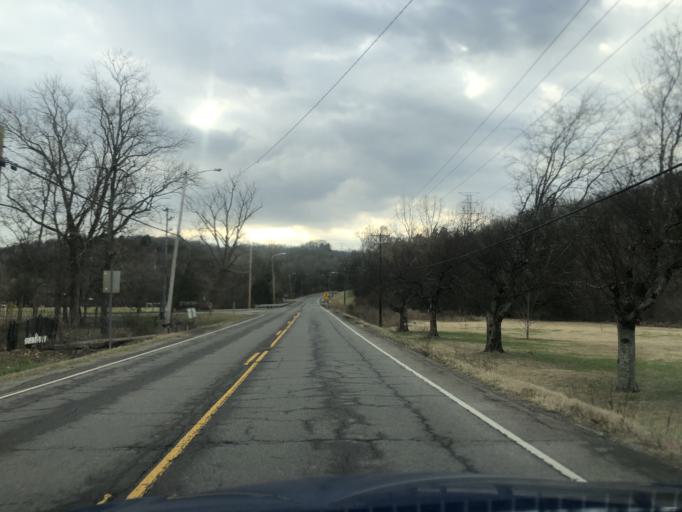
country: US
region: Tennessee
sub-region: Davidson County
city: Belle Meade
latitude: 36.1100
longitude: -86.9330
